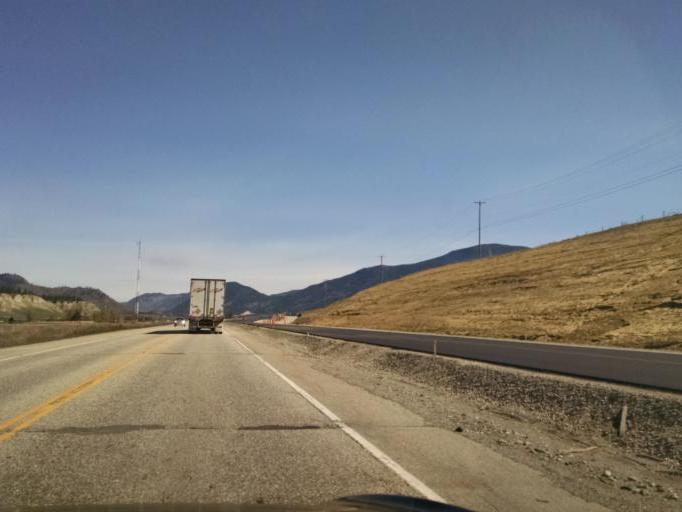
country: CA
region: British Columbia
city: Chase
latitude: 50.6669
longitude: -119.8577
